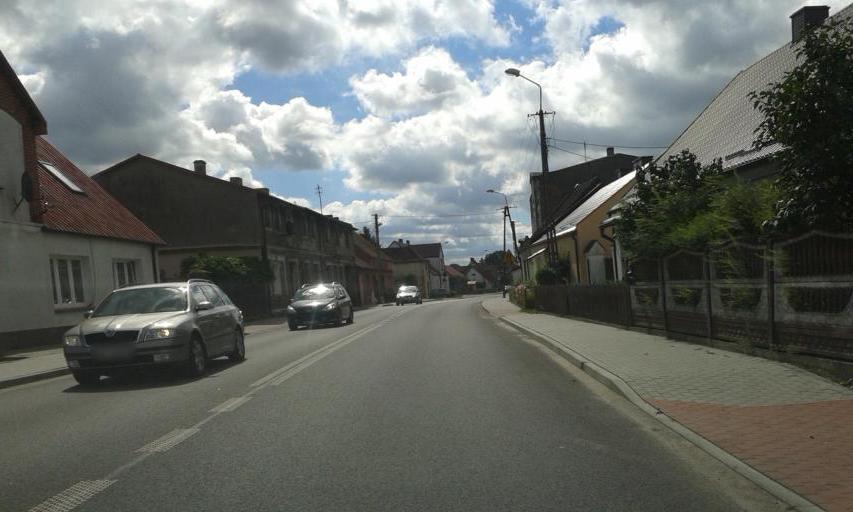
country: PL
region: West Pomeranian Voivodeship
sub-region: Powiat drawski
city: Czaplinek
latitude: 53.5258
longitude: 16.3084
